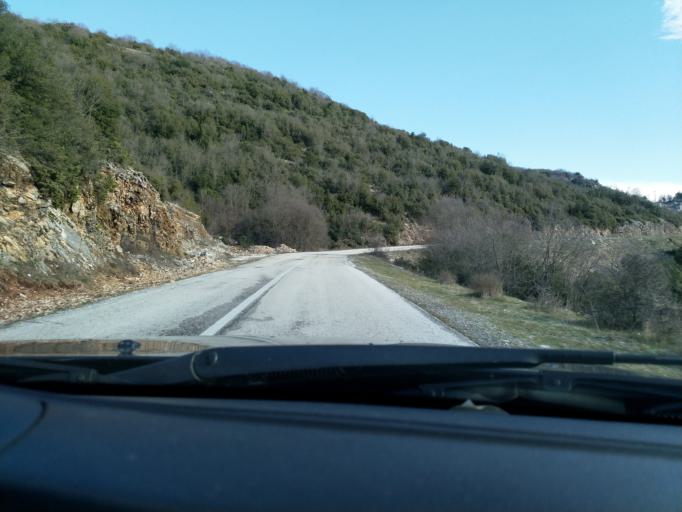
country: GR
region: Epirus
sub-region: Nomos Ioanninon
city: Asprangeloi
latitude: 39.8708
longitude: 20.7415
